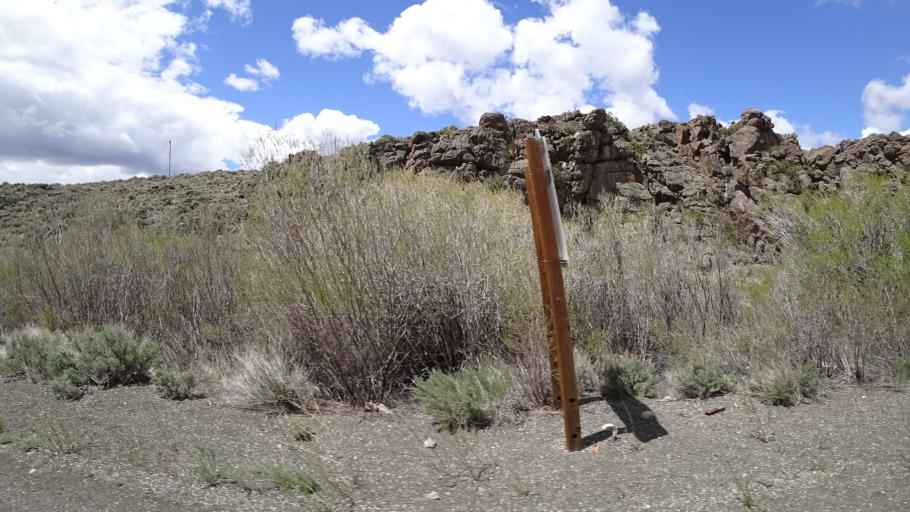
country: US
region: California
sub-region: Mono County
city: Bridgeport
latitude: 38.1761
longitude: -119.1948
